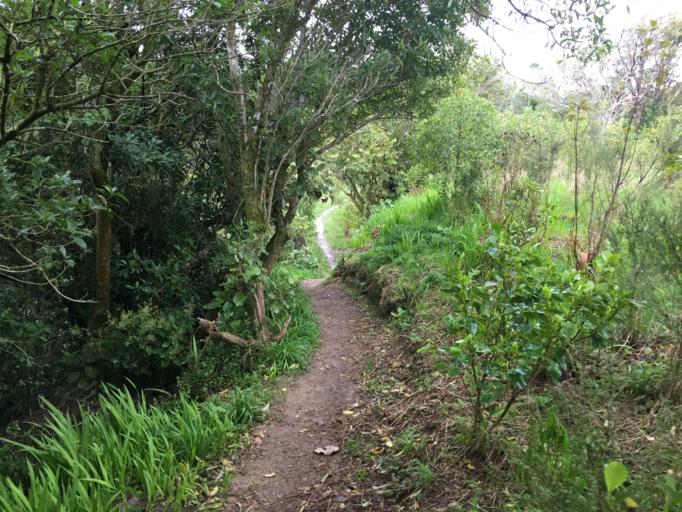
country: NZ
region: Wellington
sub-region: Wellington City
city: Kelburn
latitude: -41.2757
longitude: 174.7646
